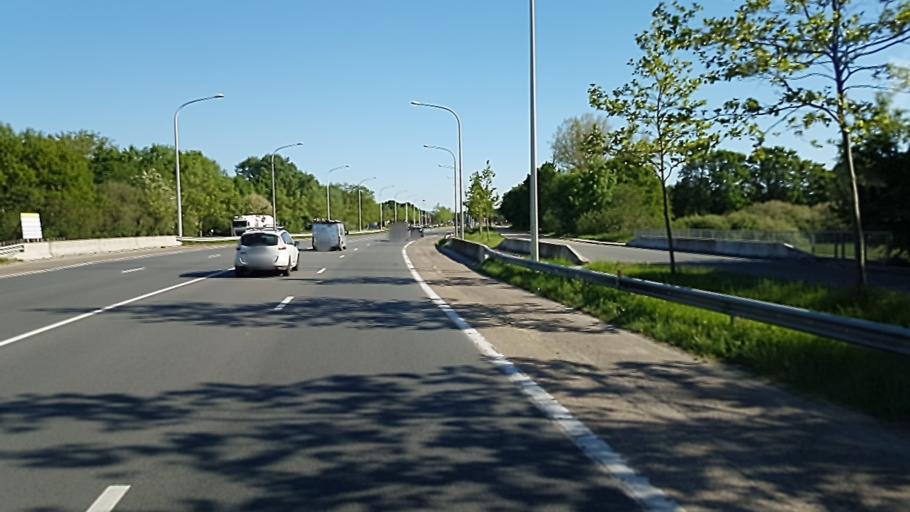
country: BE
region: Flanders
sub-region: Provincie Antwerpen
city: Herentals
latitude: 51.1839
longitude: 4.8480
